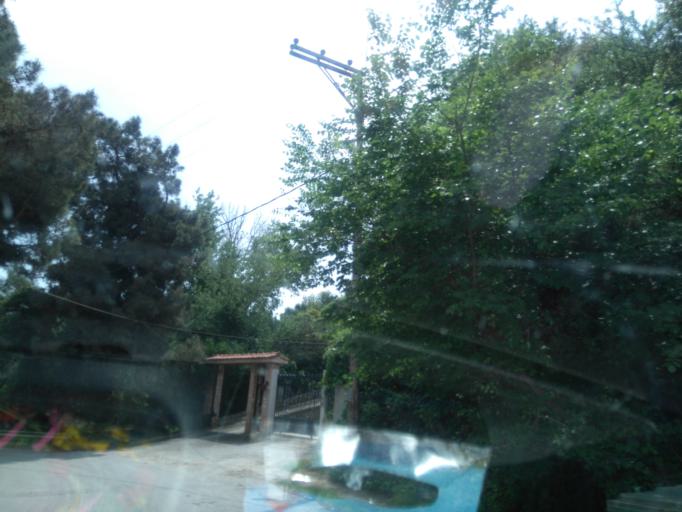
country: GR
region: Central Macedonia
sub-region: Nomos Thessalonikis
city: Lagyna
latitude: 40.7245
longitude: 22.9945
